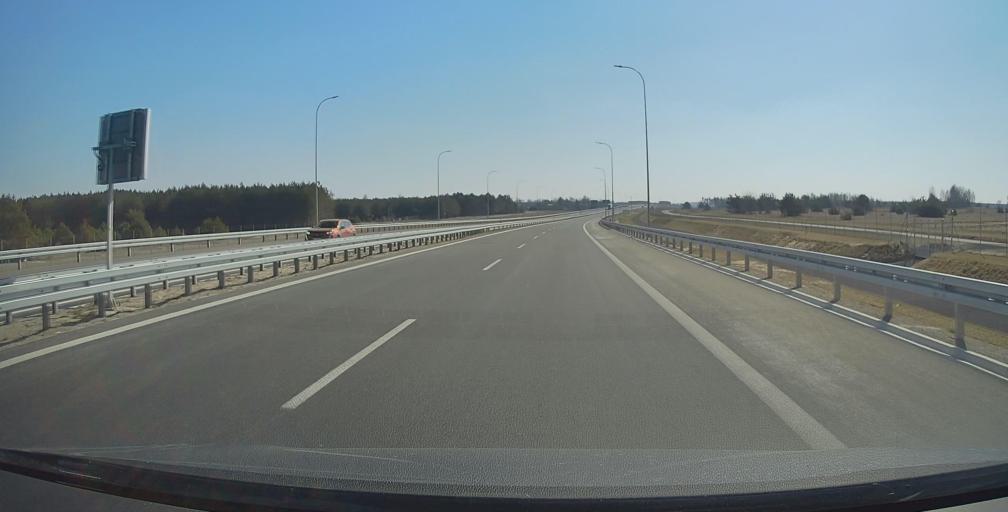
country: PL
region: Subcarpathian Voivodeship
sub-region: Powiat nizanski
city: Jezowe
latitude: 50.3762
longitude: 22.1787
